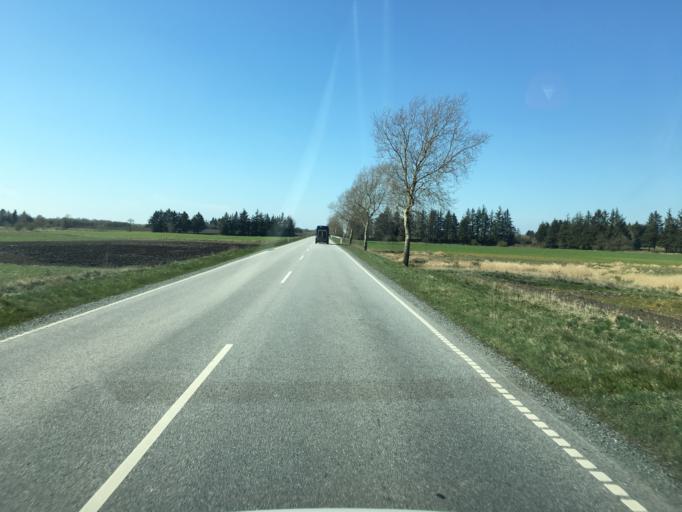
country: DK
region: South Denmark
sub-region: Aabenraa Kommune
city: Tinglev
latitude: 54.9492
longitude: 9.3478
